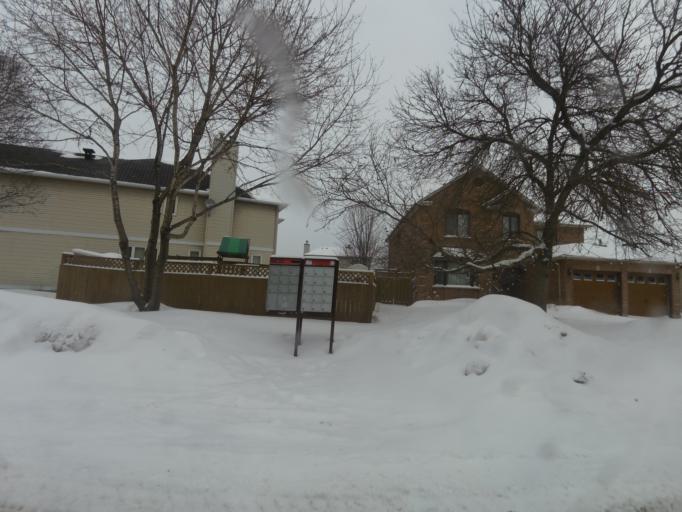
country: CA
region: Ontario
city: Ottawa
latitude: 45.3753
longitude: -75.6148
